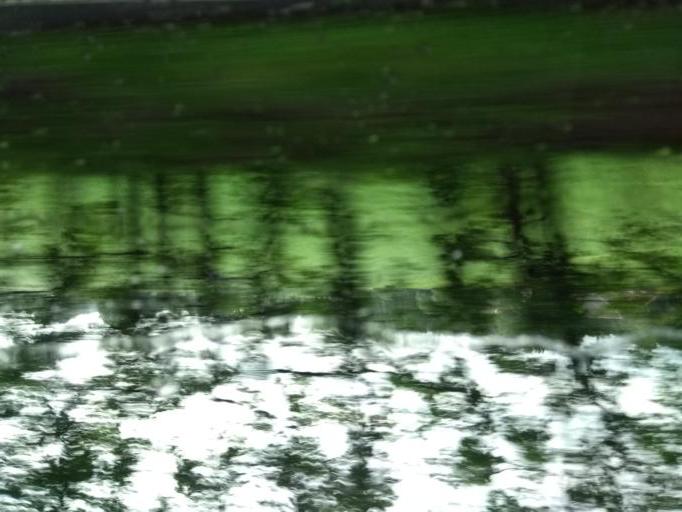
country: NL
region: Overijssel
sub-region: Gemeente Twenterand
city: Vroomshoop
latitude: 52.5023
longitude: 6.5732
